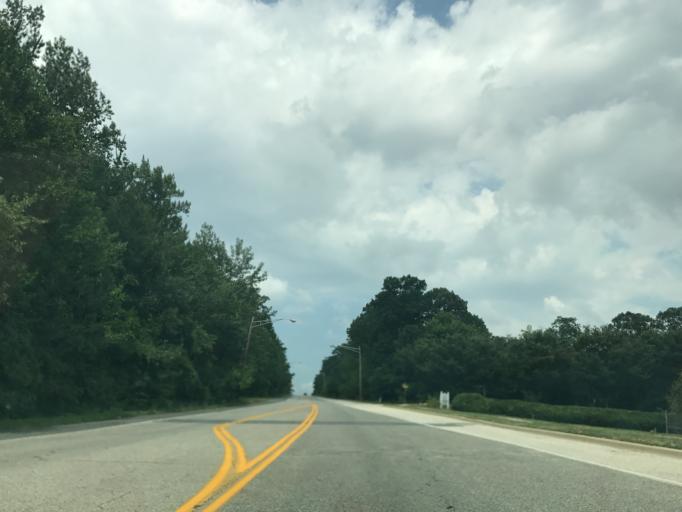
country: US
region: Maryland
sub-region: Anne Arundel County
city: Ferndale
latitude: 39.1947
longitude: -76.6184
